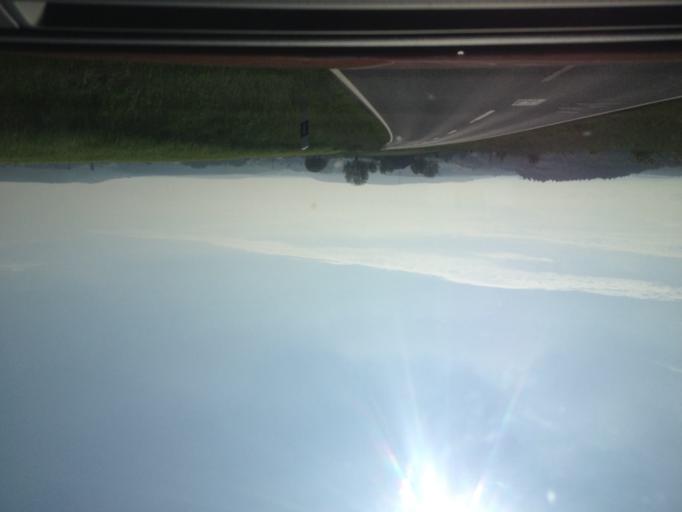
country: DE
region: Bavaria
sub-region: Upper Palatinate
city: Kirchenthumbach
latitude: 49.7576
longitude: 11.7065
